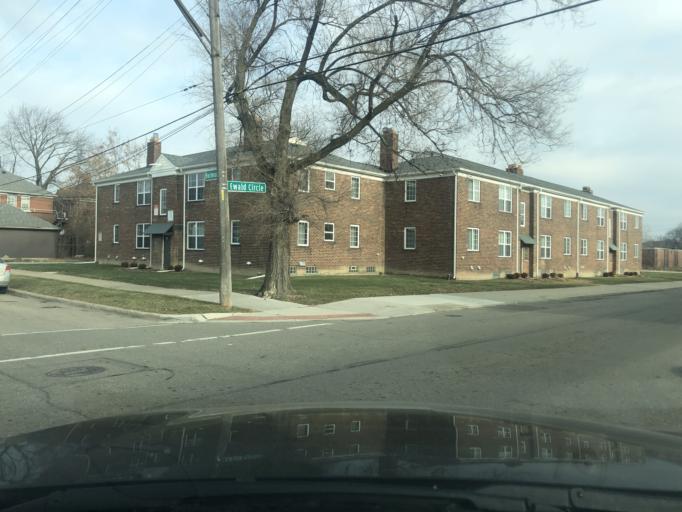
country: US
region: Michigan
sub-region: Wayne County
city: Highland Park
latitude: 42.3929
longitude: -83.1360
